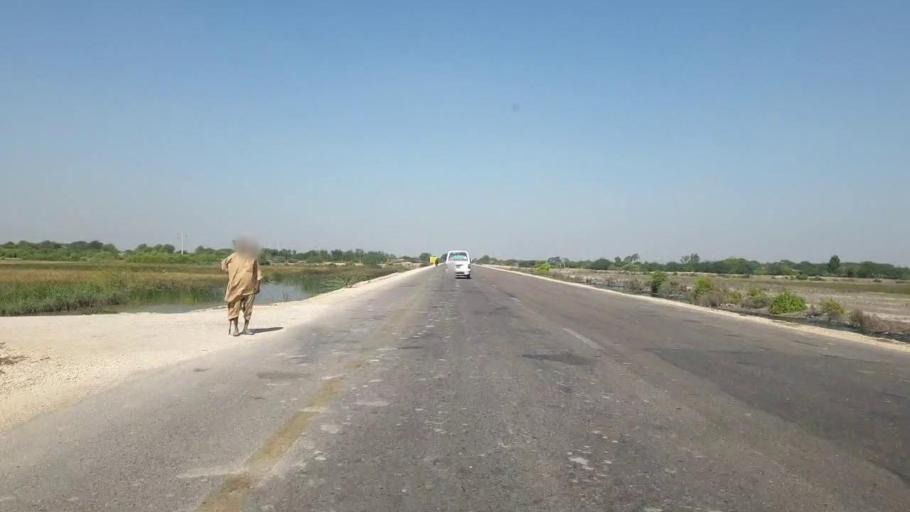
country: PK
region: Sindh
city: Talhar
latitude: 24.8263
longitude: 68.8159
